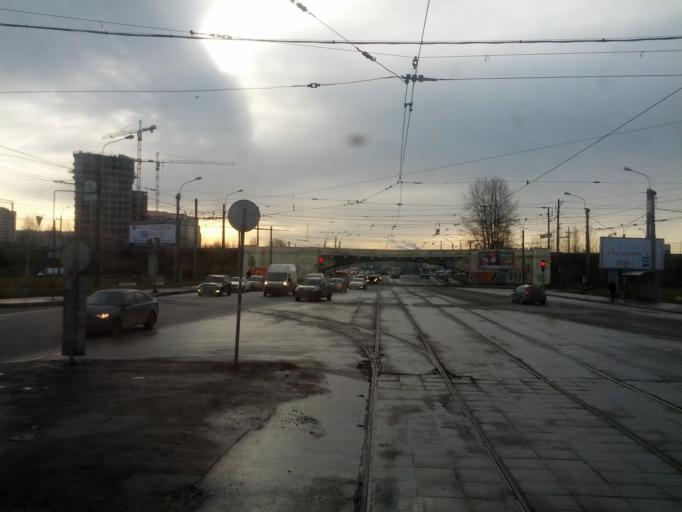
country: RU
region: St.-Petersburg
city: Centralniy
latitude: 59.9202
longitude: 30.4224
